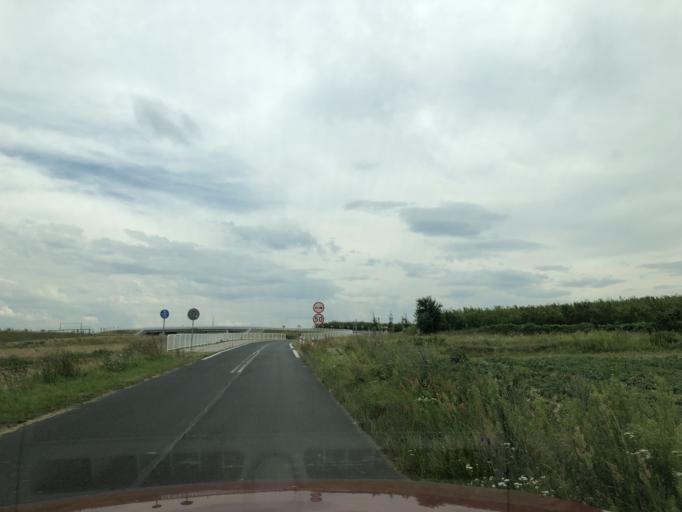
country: PL
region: Lower Silesian Voivodeship
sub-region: Powiat trzebnicki
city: Trzebnica
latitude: 51.3203
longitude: 17.0328
